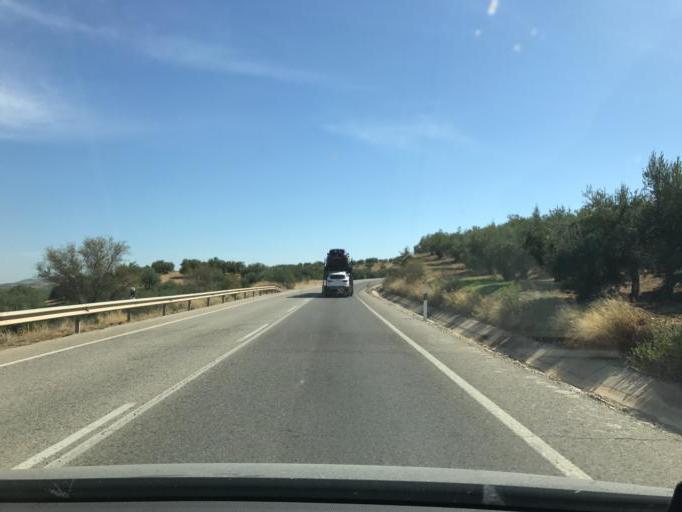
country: ES
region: Andalusia
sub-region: Province of Cordoba
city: Luque
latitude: 37.5678
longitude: -4.2392
